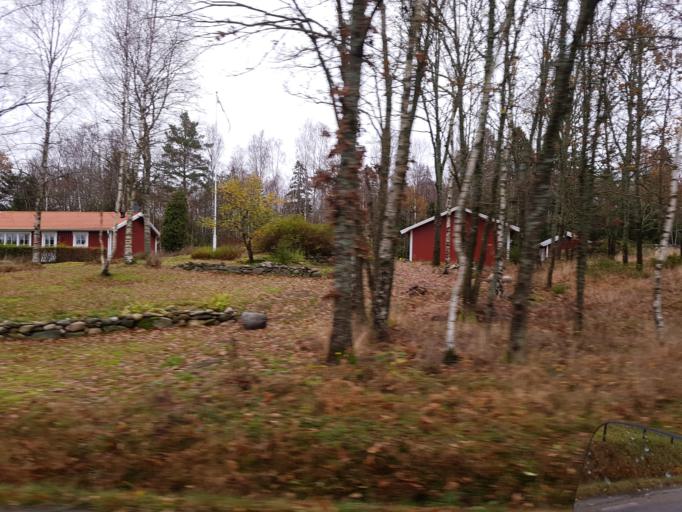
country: SE
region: Vaestra Goetaland
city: Svanesund
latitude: 58.1575
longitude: 11.7832
